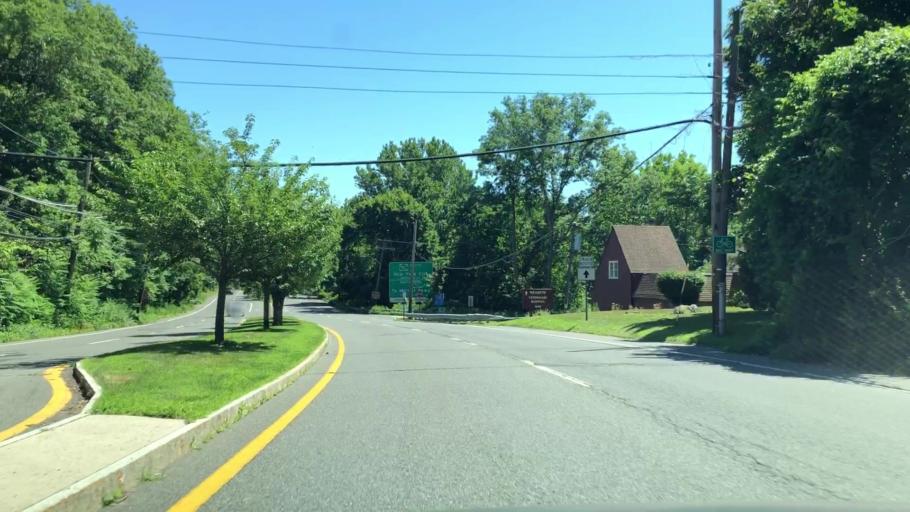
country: US
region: New York
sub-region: Westchester County
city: Harrison
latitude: 40.9893
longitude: -73.7459
